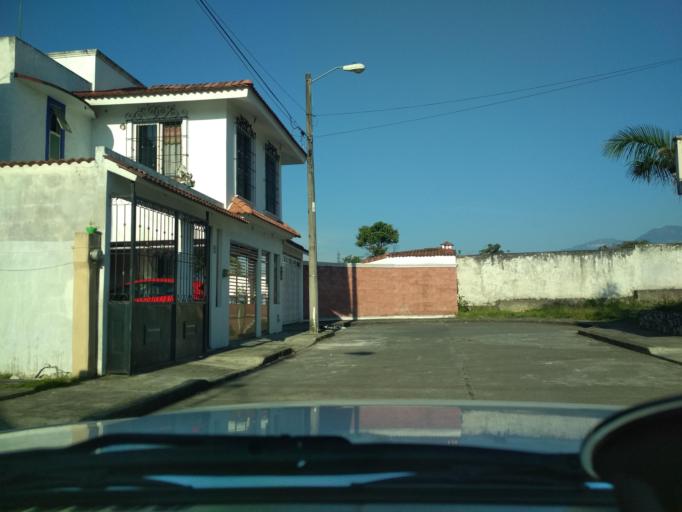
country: MX
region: Veracruz
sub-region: Fortin
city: Fraccionamiento Villas de la Llave
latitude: 18.9190
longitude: -96.9939
